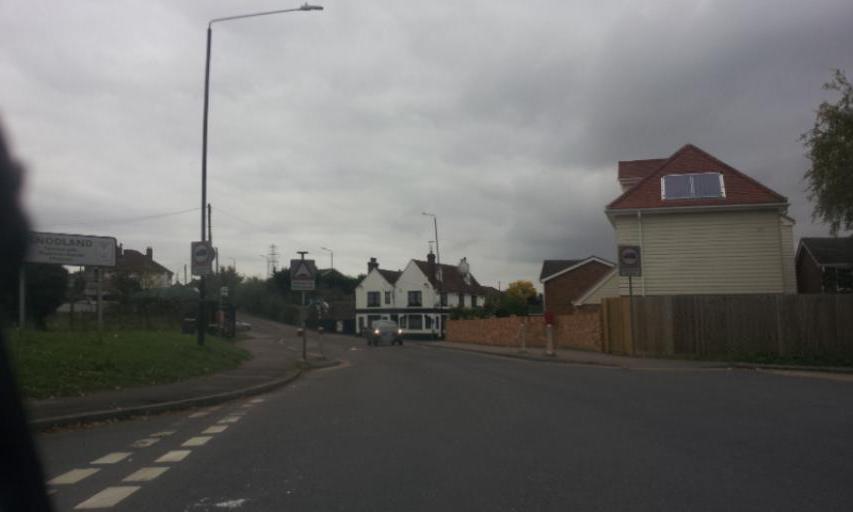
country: GB
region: England
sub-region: Kent
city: Snodland
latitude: 51.3190
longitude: 0.4355
